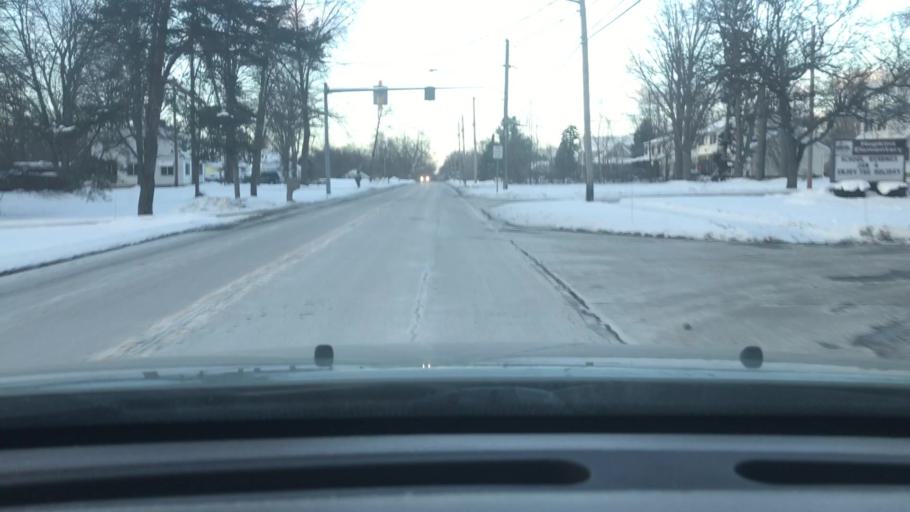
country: US
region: Ohio
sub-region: Lake County
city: Mentor
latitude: 41.6642
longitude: -81.3157
